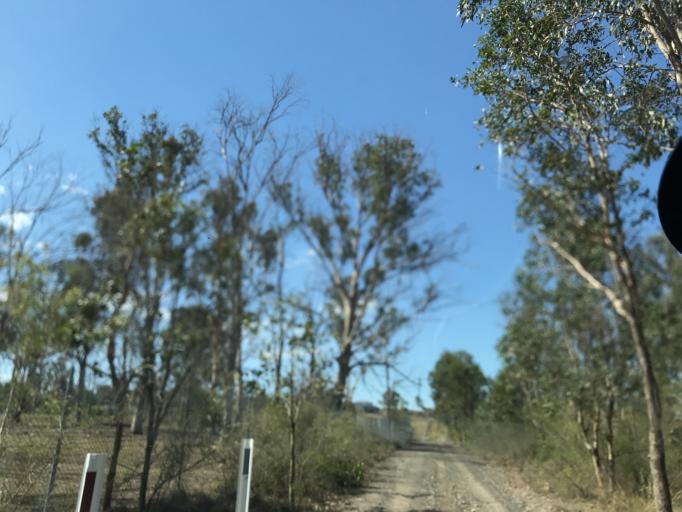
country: AU
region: New South Wales
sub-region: Penrith Municipality
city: Kingswood Park
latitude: -33.7975
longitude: 150.7366
